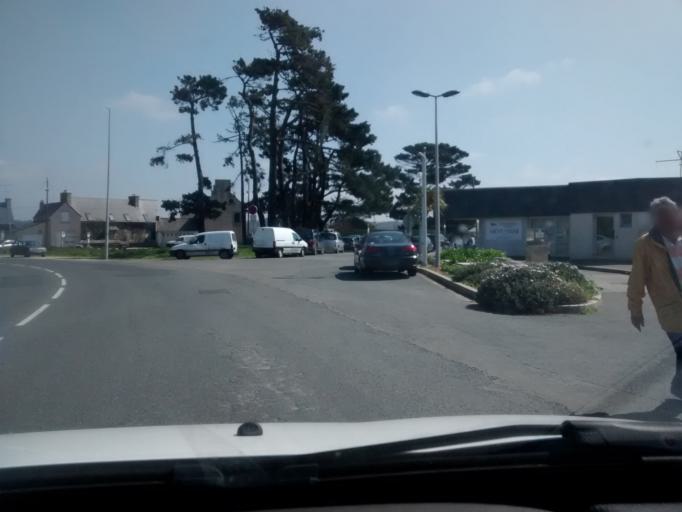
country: FR
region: Brittany
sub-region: Departement des Cotes-d'Armor
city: Perros-Guirec
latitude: 48.8062
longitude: -3.4387
